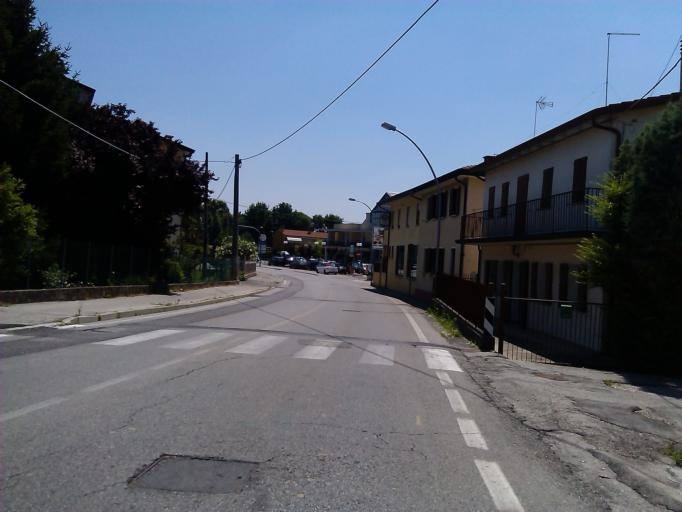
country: IT
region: Veneto
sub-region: Provincia di Padova
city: Camposampiero
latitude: 45.5626
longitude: 11.9375
